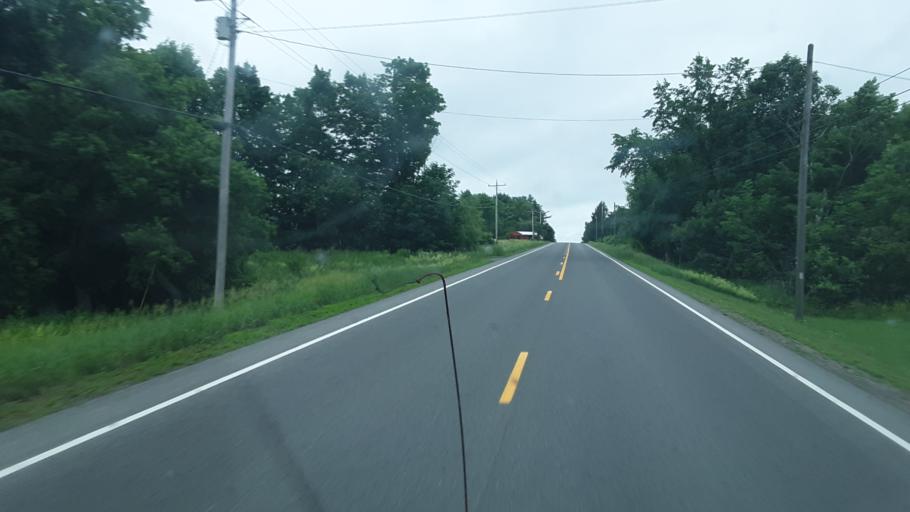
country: US
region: Maine
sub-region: Penobscot County
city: Patten
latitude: 45.9630
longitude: -68.4515
